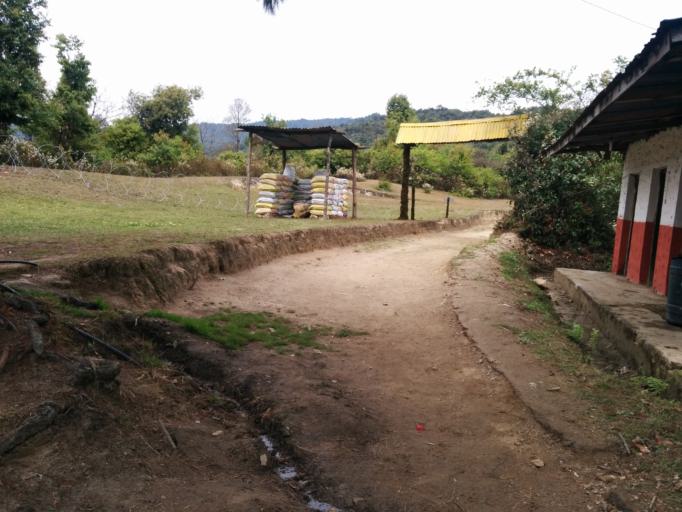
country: NP
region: Central Region
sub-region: Bagmati Zone
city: Nagarkot
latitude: 27.7849
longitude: 85.4350
